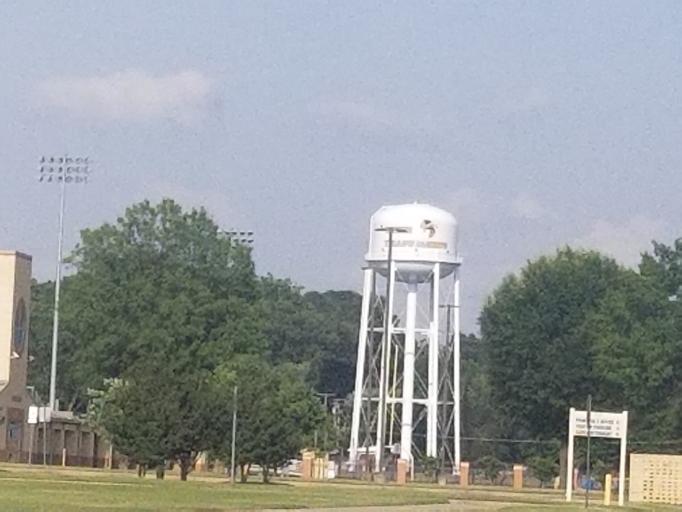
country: US
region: Arkansas
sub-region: Cross County
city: Wynne
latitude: 35.2286
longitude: -90.7856
